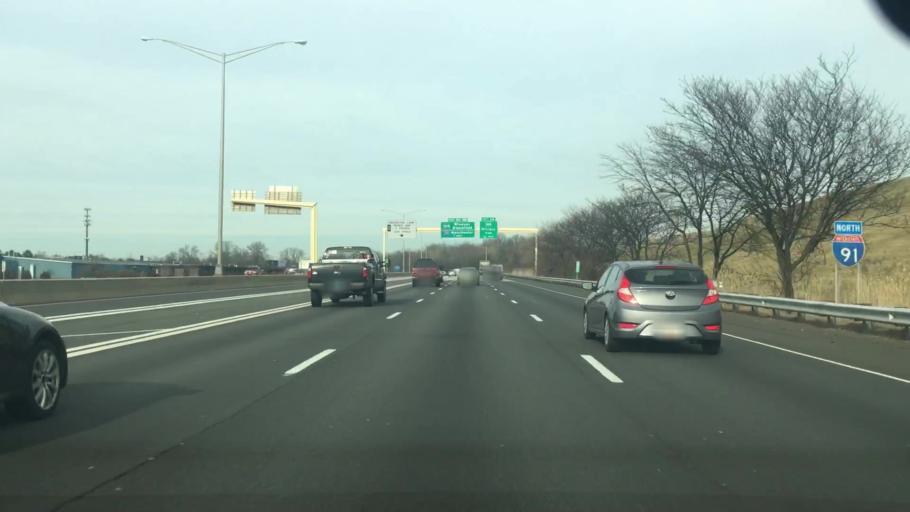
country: US
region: Connecticut
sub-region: Hartford County
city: East Hartford
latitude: 41.7948
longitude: -72.6533
